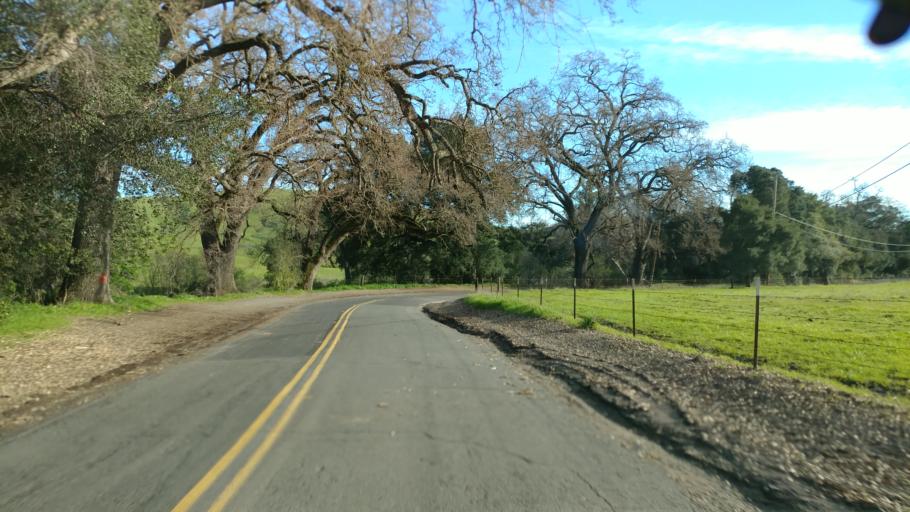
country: US
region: California
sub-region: Contra Costa County
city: Blackhawk
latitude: 37.8130
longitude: -121.8575
